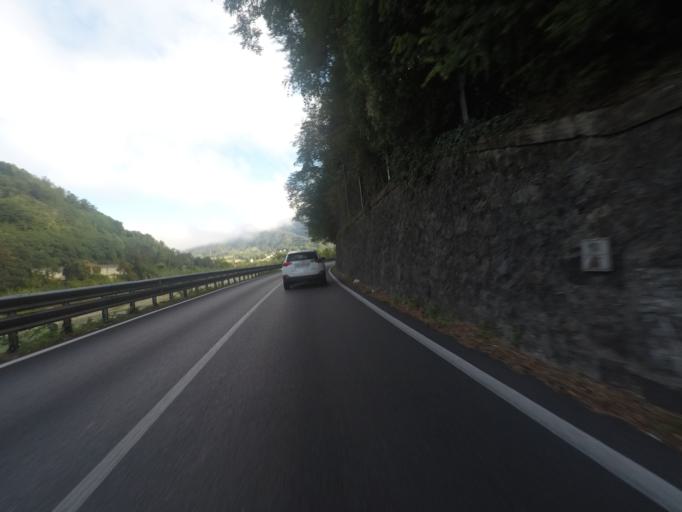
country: IT
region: Tuscany
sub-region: Provincia di Lucca
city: Bagni di Lucca
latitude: 43.9922
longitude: 10.5536
